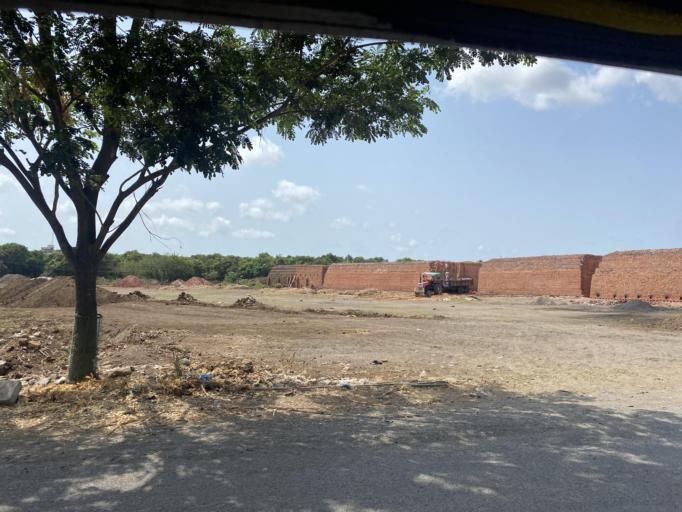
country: IN
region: Gujarat
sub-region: Valsad
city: Vapi
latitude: 20.2802
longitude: 72.8703
